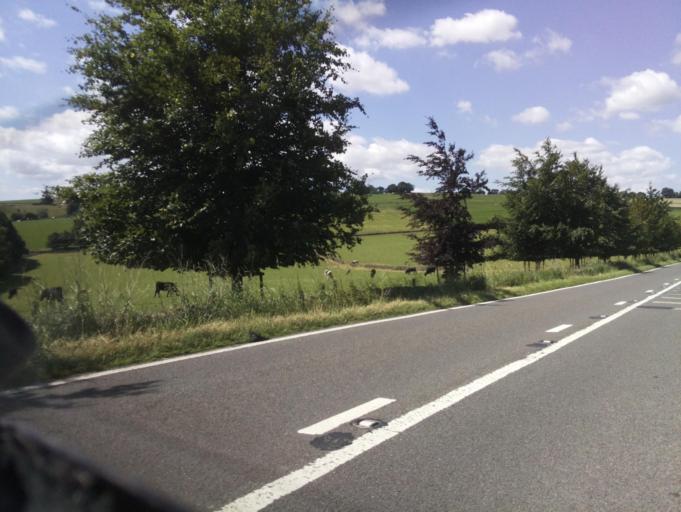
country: GB
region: England
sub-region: Derbyshire
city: Ashbourne
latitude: 53.0713
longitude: -1.7506
